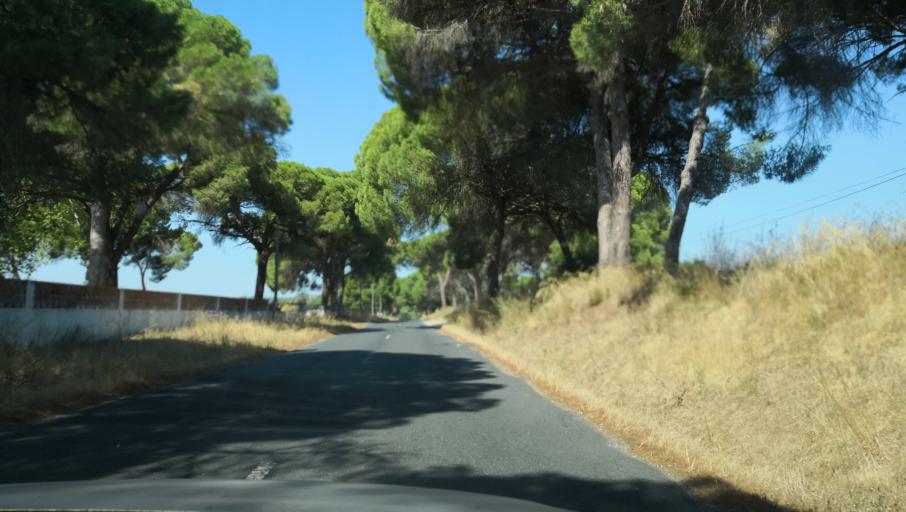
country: PT
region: Setubal
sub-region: Alcacer do Sal
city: Alcacer do Sal
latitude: 38.2804
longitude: -8.3966
